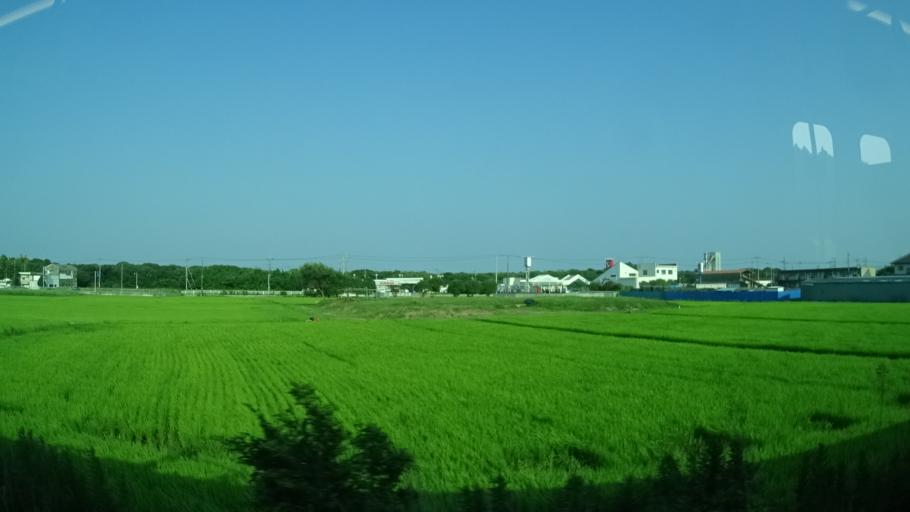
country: JP
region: Ibaraki
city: Takahagi
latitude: 36.7490
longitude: 140.7274
